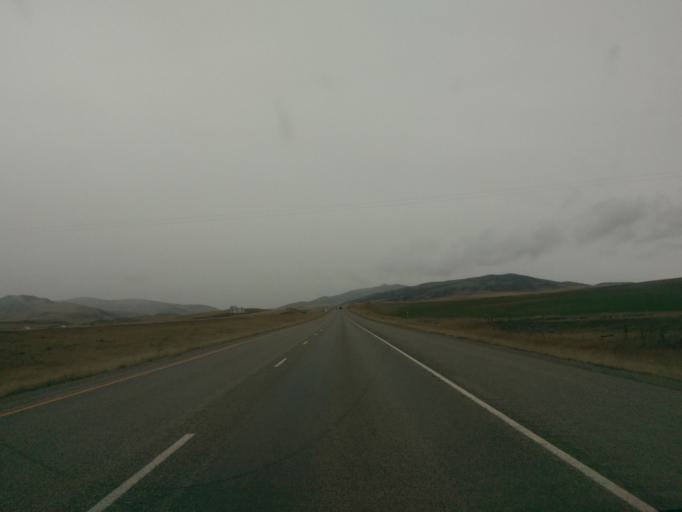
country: US
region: Montana
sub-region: Gallatin County
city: Three Forks
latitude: 45.9136
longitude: -111.7628
